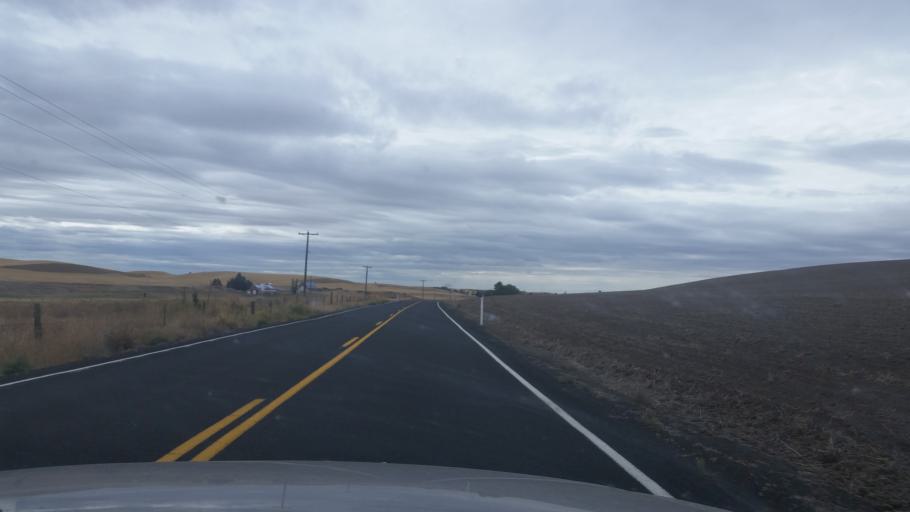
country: US
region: Washington
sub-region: Spokane County
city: Medical Lake
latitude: 47.5193
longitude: -117.9275
